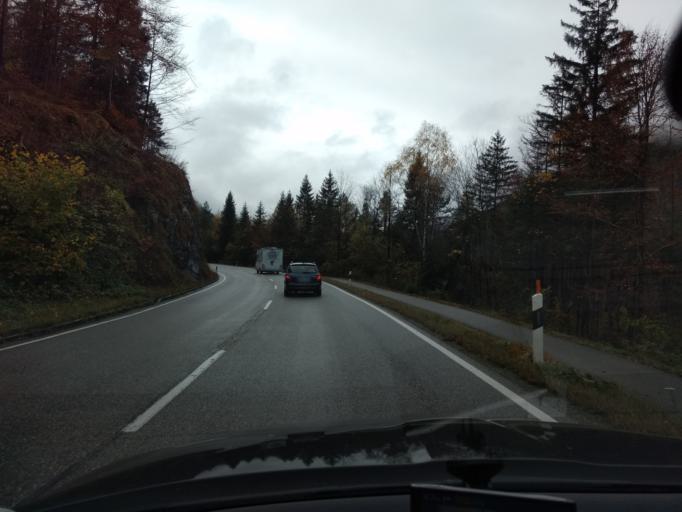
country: DE
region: Bavaria
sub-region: Upper Bavaria
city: Lenggries
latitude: 47.6119
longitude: 11.5856
